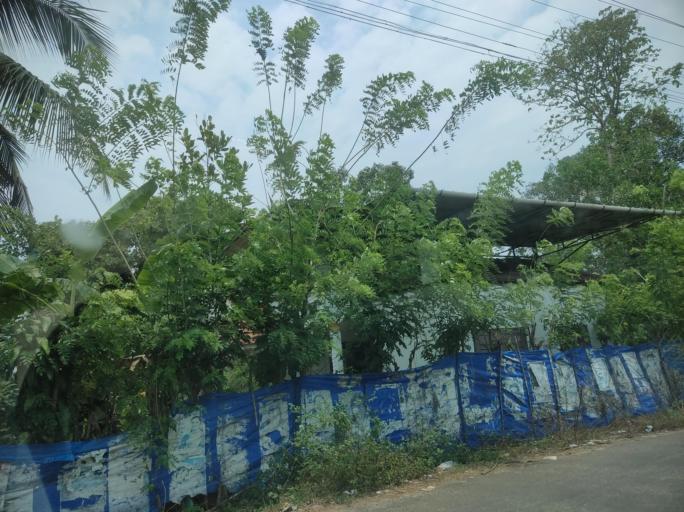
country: IN
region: Kerala
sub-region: Alappuzha
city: Kutiatodu
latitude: 9.7516
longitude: 76.3252
